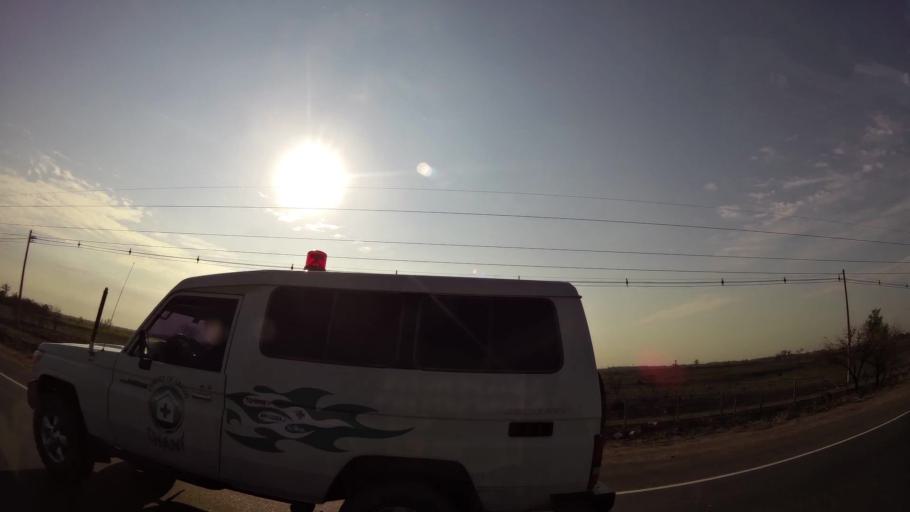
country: BO
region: Santa Cruz
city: La Belgica
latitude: -17.6424
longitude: -63.1575
